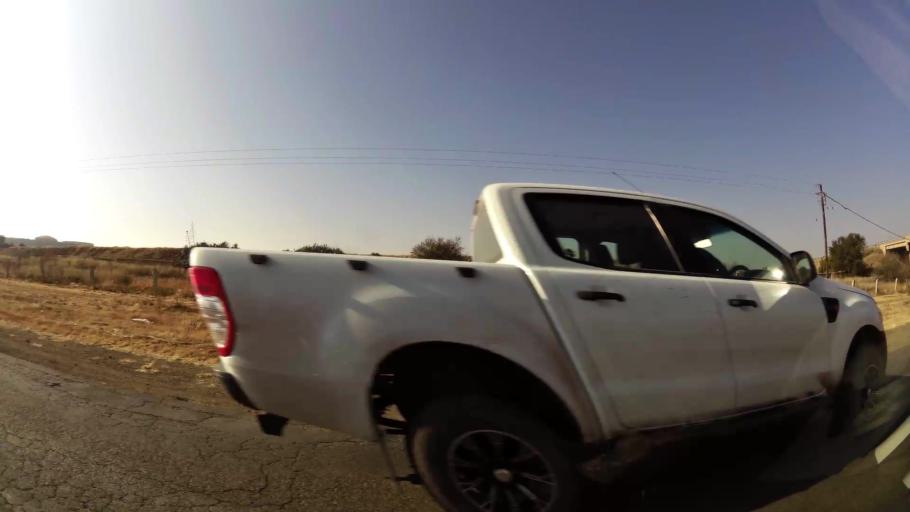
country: ZA
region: Orange Free State
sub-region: Mangaung Metropolitan Municipality
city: Bloemfontein
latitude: -29.1794
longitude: 26.1903
